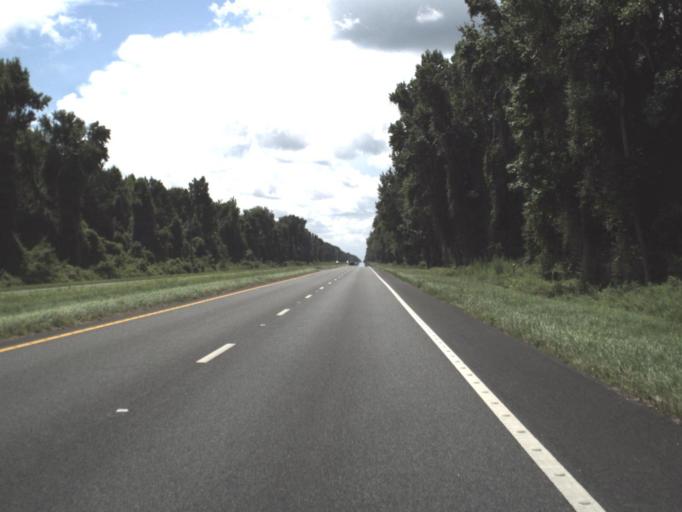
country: US
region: Florida
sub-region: Taylor County
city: Perry
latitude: 30.2841
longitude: -83.7309
